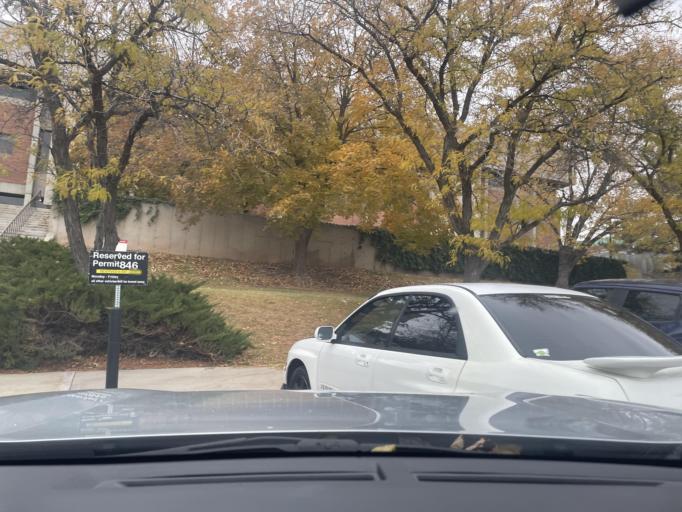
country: US
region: Utah
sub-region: Salt Lake County
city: Salt Lake City
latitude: 40.7607
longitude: -111.8455
